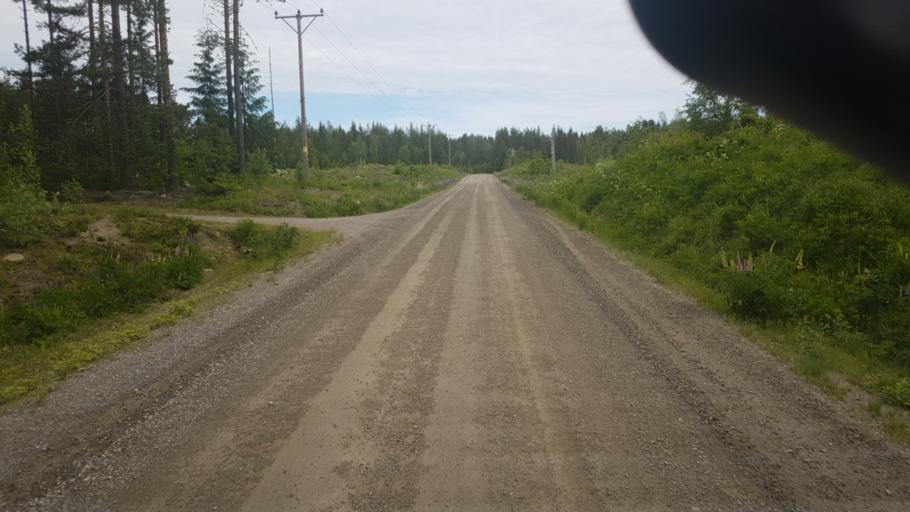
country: SE
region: Vaermland
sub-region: Arvika Kommun
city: Arvika
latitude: 59.8661
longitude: 12.7127
